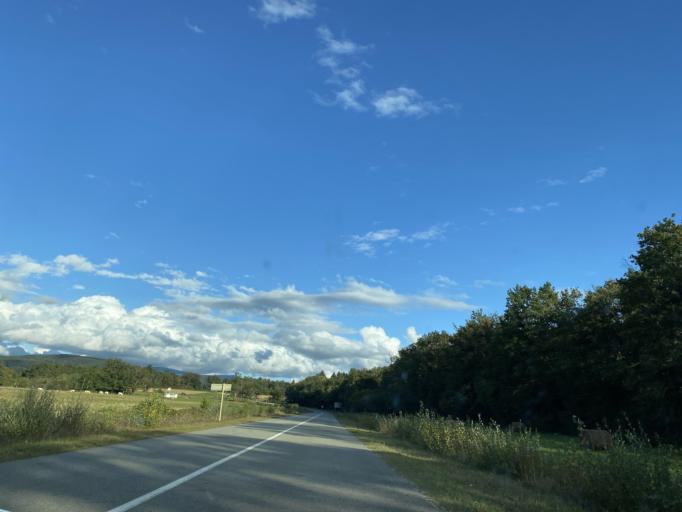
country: FR
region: Auvergne
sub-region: Departement du Puy-de-Dome
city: Puy-Guillaume
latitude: 45.9478
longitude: 3.4768
